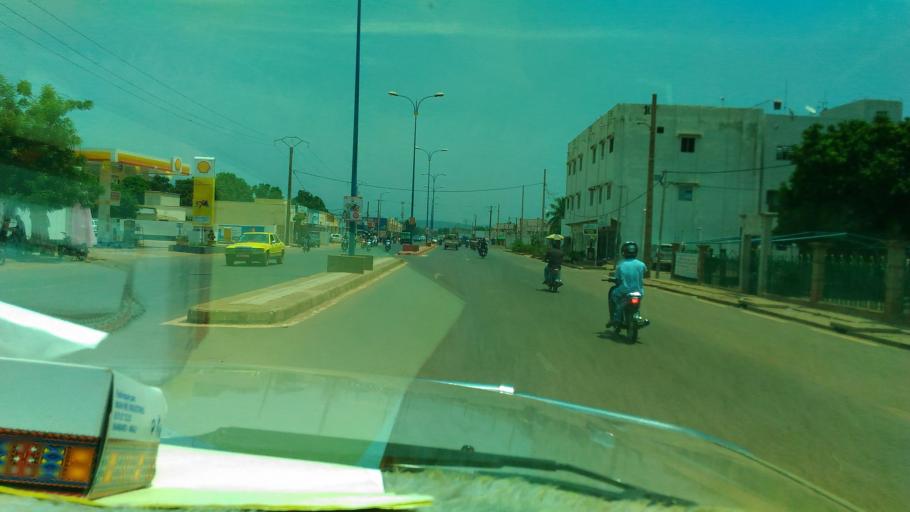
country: ML
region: Bamako
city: Bamako
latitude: 12.6071
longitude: -8.0471
